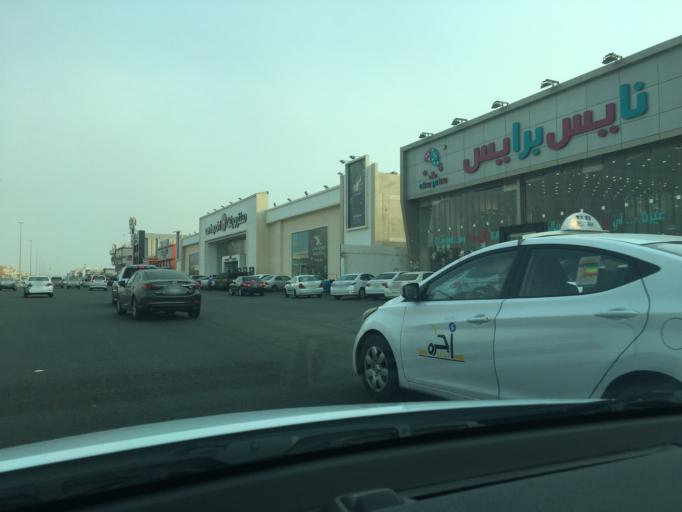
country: SA
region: Makkah
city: Jeddah
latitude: 21.7594
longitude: 39.1842
